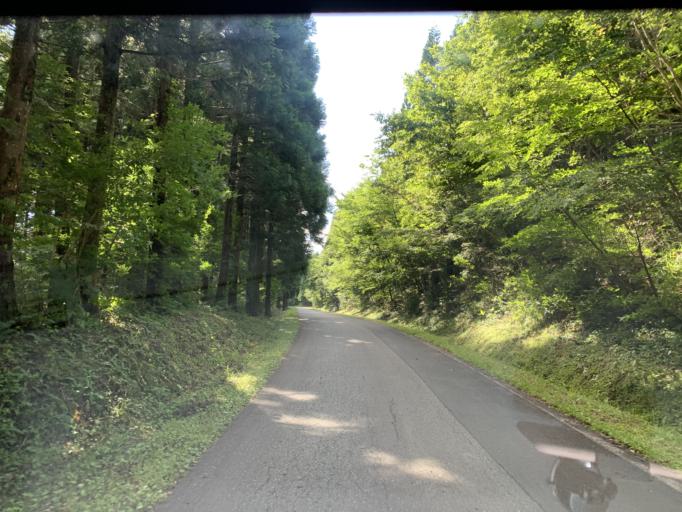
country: JP
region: Iwate
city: Ichinoseki
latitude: 38.9264
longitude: 140.9356
